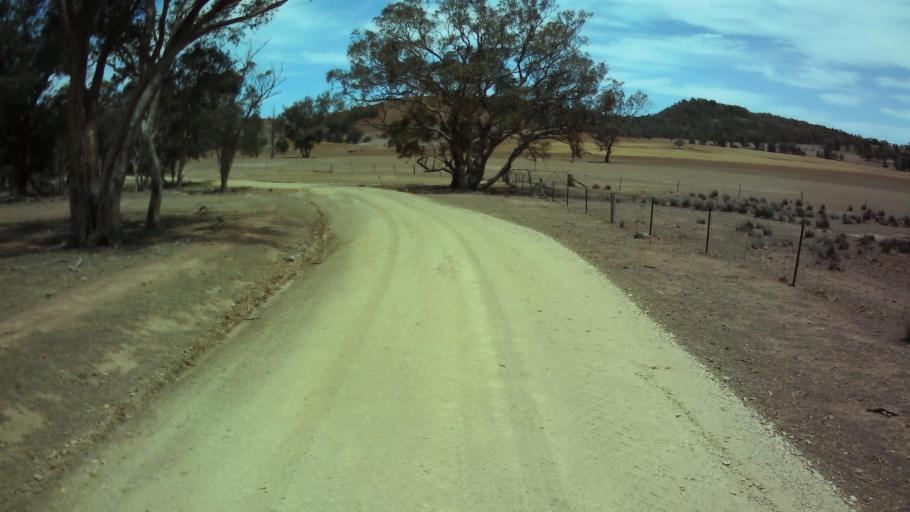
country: AU
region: New South Wales
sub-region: Weddin
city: Grenfell
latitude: -33.7833
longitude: 148.1516
